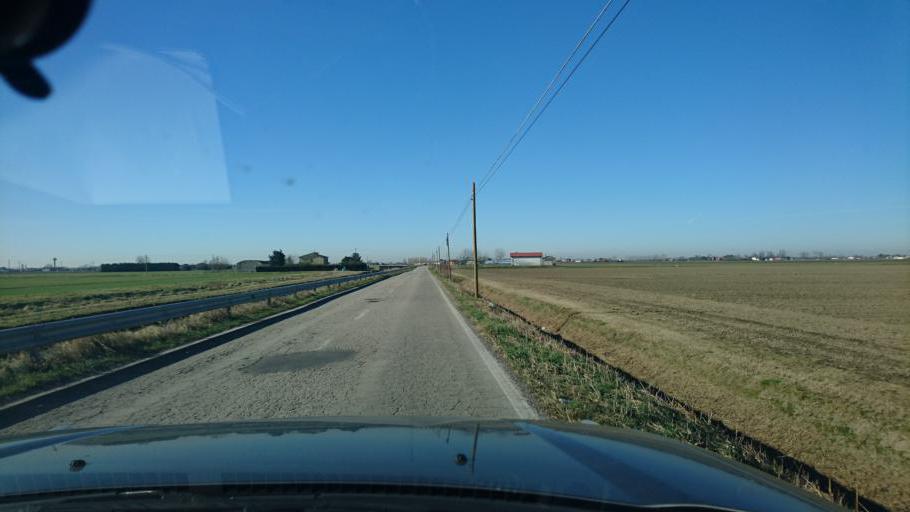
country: IT
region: Emilia-Romagna
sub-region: Provincia di Ferrara
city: Mesola
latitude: 44.9446
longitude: 12.2441
